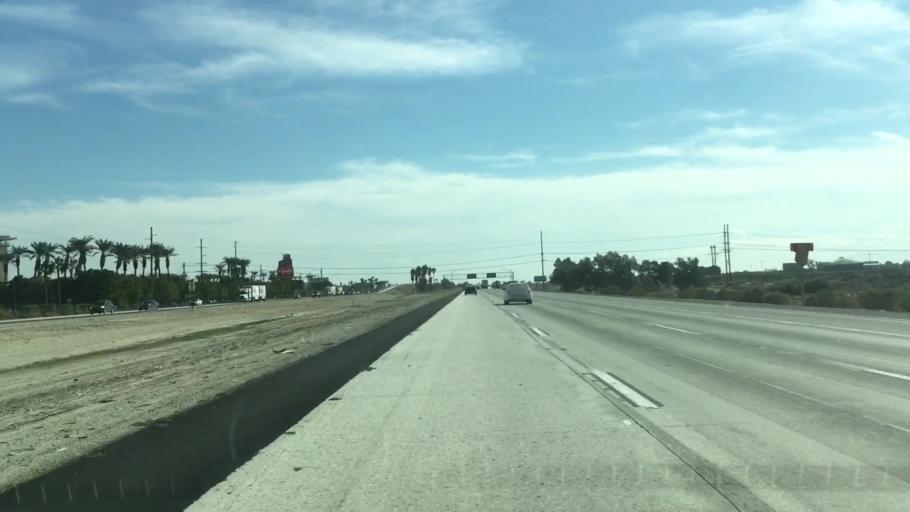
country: US
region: California
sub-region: Riverside County
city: Indio
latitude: 33.7230
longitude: -116.1985
